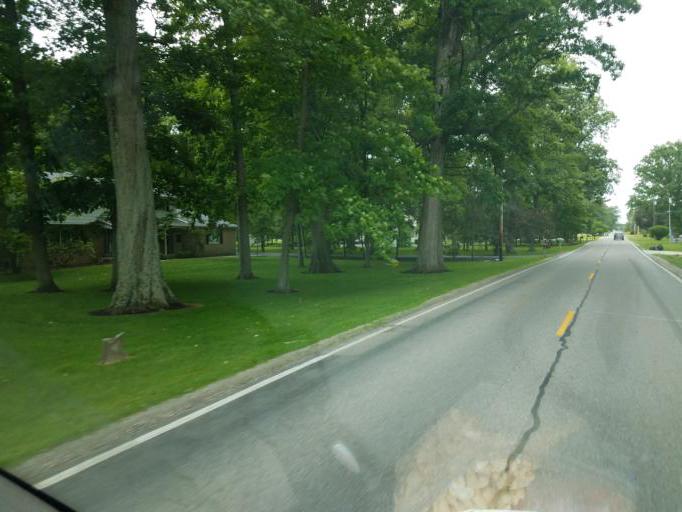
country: US
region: Ohio
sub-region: Marion County
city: Marion
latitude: 40.5495
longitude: -83.0815
